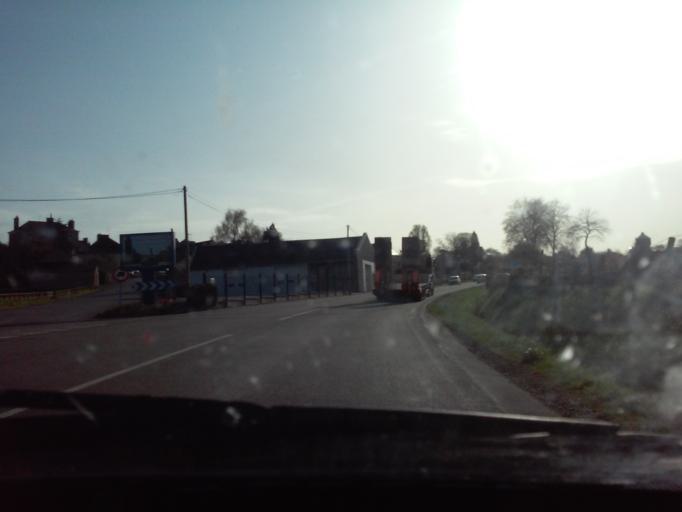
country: FR
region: Brittany
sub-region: Departement d'Ille-et-Vilaine
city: Saint-Aubin-du-Cormier
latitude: 48.2632
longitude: -1.3982
